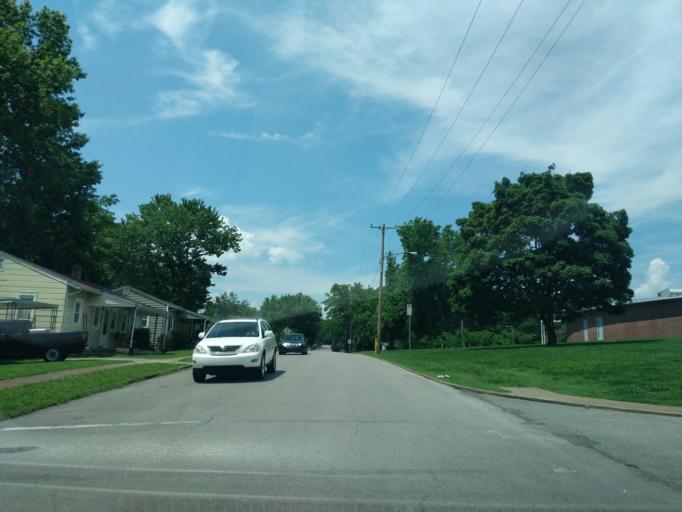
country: US
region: Tennessee
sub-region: Davidson County
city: Lakewood
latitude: 36.2503
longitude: -86.6443
